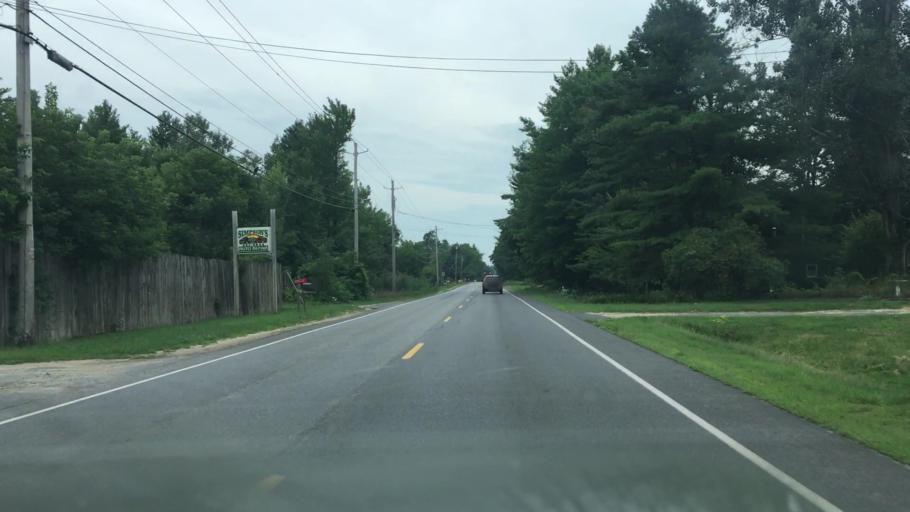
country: US
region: New York
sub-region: Clinton County
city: Plattsburgh West
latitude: 44.6577
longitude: -73.5103
